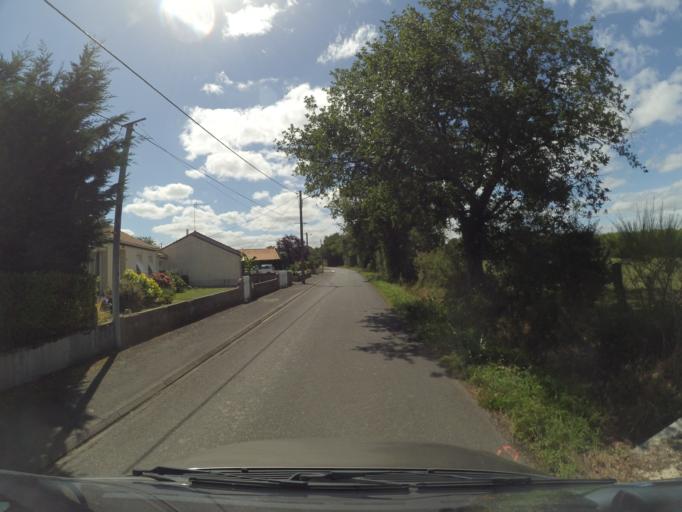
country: FR
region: Pays de la Loire
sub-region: Departement de la Loire-Atlantique
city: Saint-Hilaire-de-Clisson
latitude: 47.0583
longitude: -1.3135
